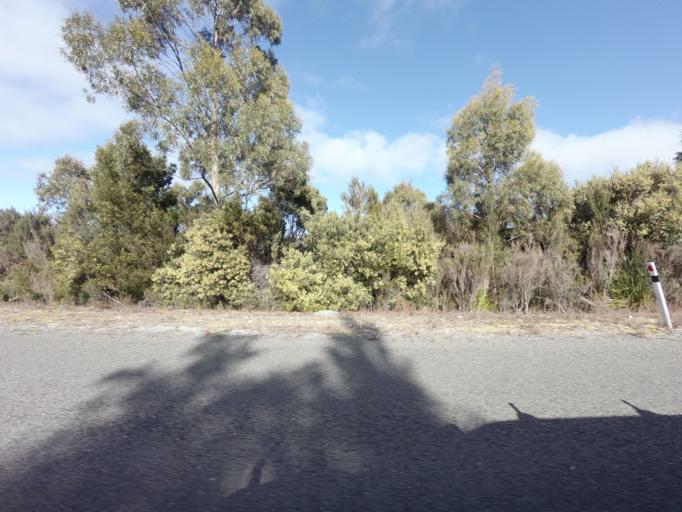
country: AU
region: Tasmania
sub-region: Huon Valley
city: Geeveston
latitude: -42.8265
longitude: 146.1254
